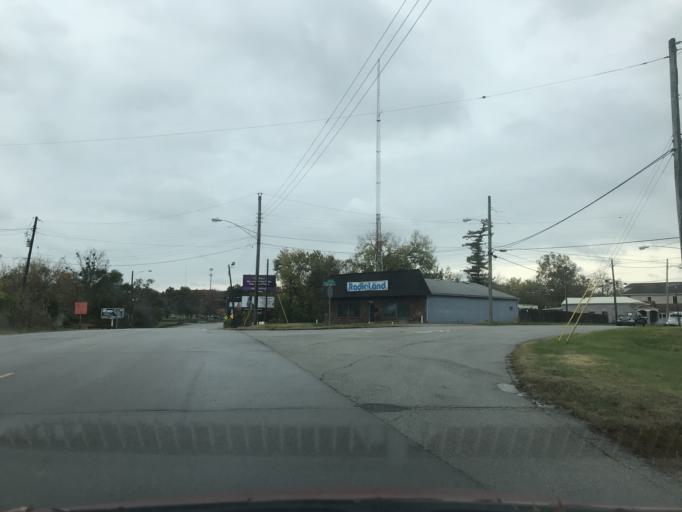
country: US
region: Indiana
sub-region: Clark County
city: Jeffersonville
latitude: 38.2505
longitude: -85.7177
